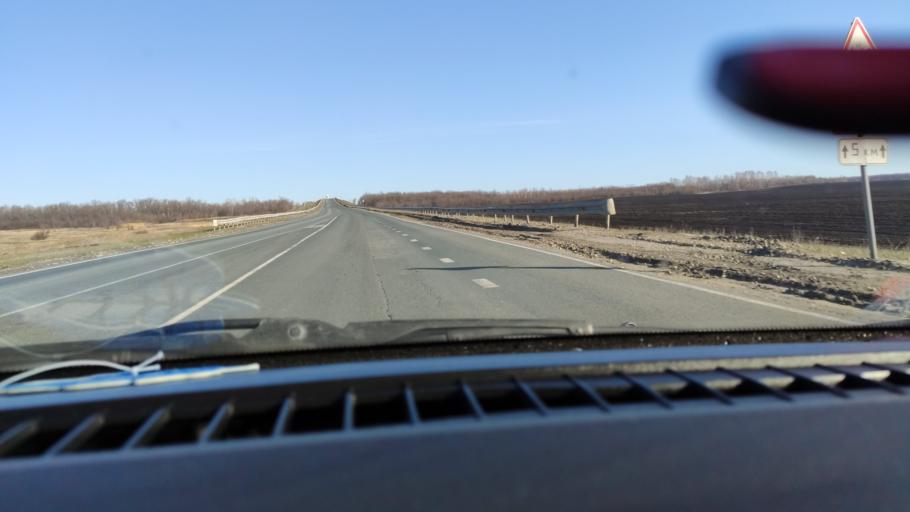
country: RU
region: Saratov
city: Dukhovnitskoye
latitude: 52.7467
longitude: 48.2514
